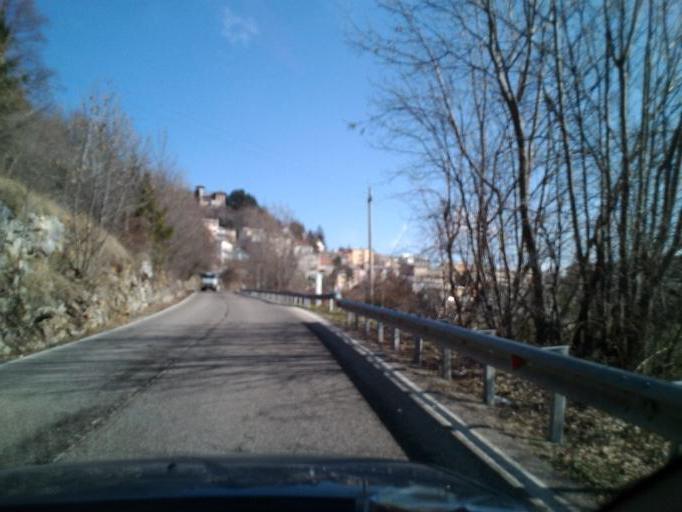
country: IT
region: Veneto
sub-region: Provincia di Verona
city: Bosco Chiesanuova
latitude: 45.6169
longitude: 11.0313
